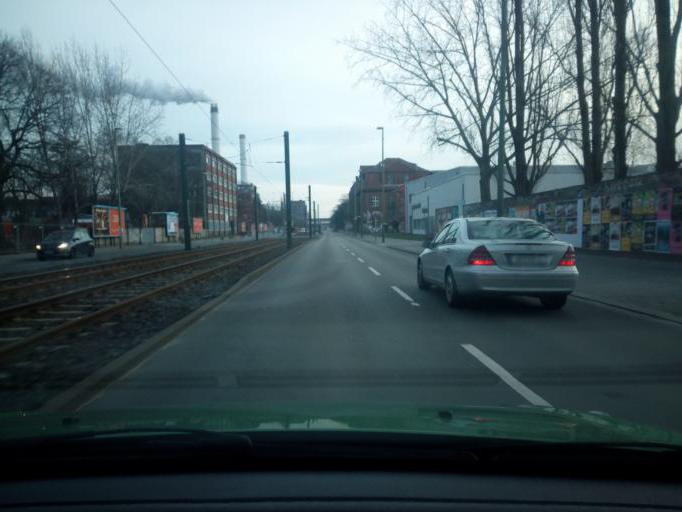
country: DE
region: Berlin
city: Rummelsburg
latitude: 52.4944
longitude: 13.4893
